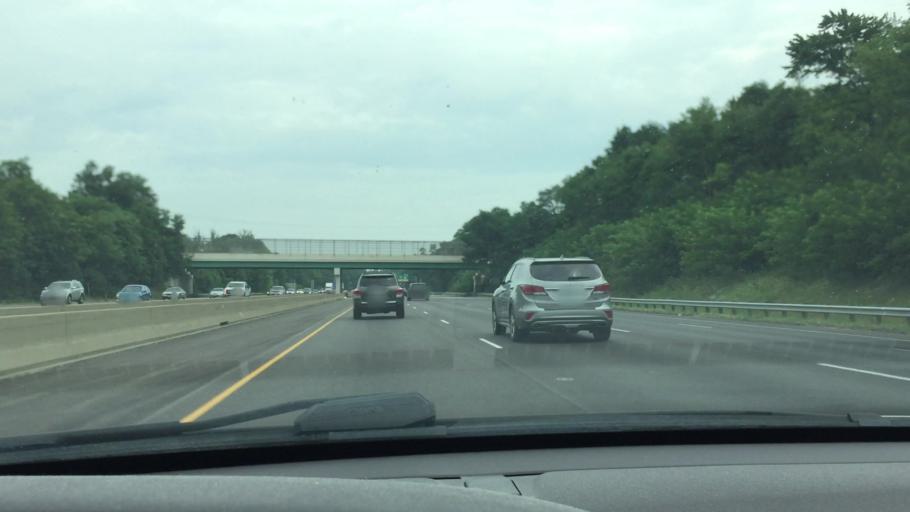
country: US
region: Ohio
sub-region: Hamilton County
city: Highpoint
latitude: 39.2598
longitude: -84.3606
